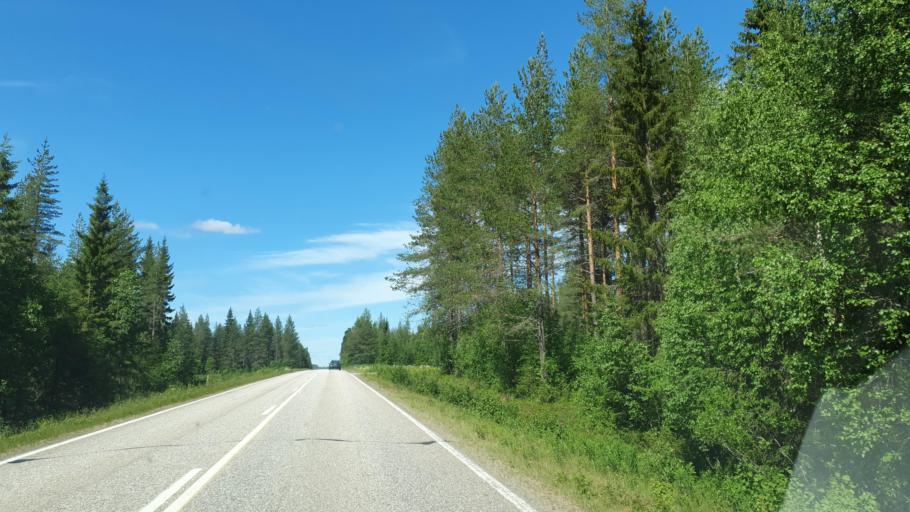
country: FI
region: Kainuu
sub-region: Kehys-Kainuu
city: Hyrynsalmi
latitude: 64.5895
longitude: 28.7636
